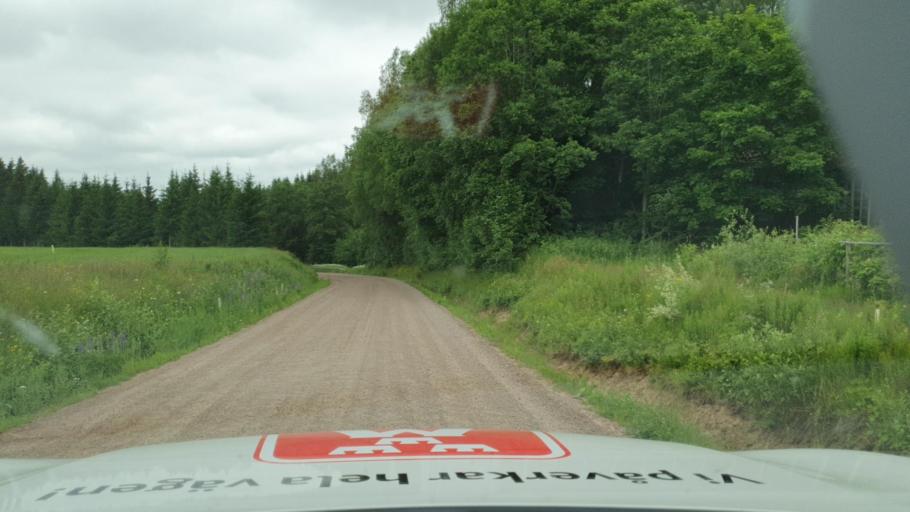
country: SE
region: Vaermland
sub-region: Filipstads Kommun
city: Filipstad
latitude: 59.5579
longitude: 13.9781
